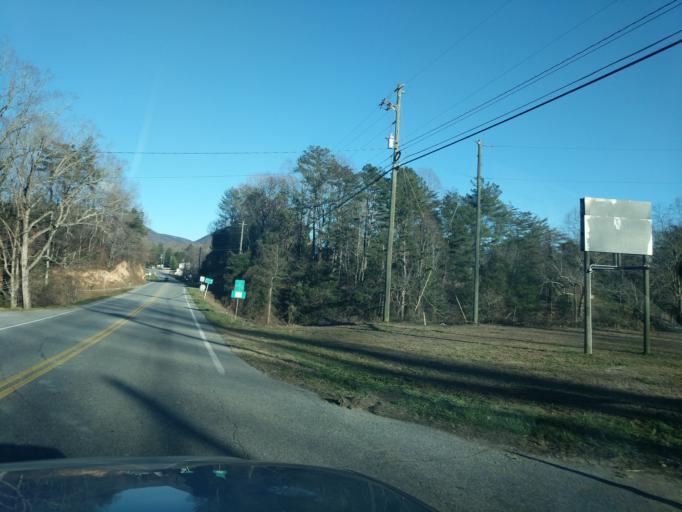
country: US
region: Georgia
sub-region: Rabun County
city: Clayton
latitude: 34.8807
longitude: -83.4193
